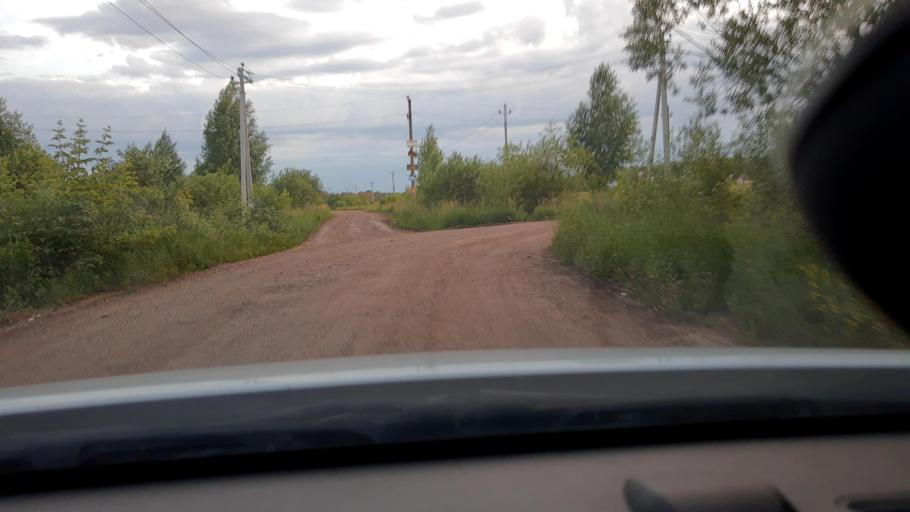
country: RU
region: Bashkortostan
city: Kabakovo
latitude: 54.4425
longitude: 55.9126
